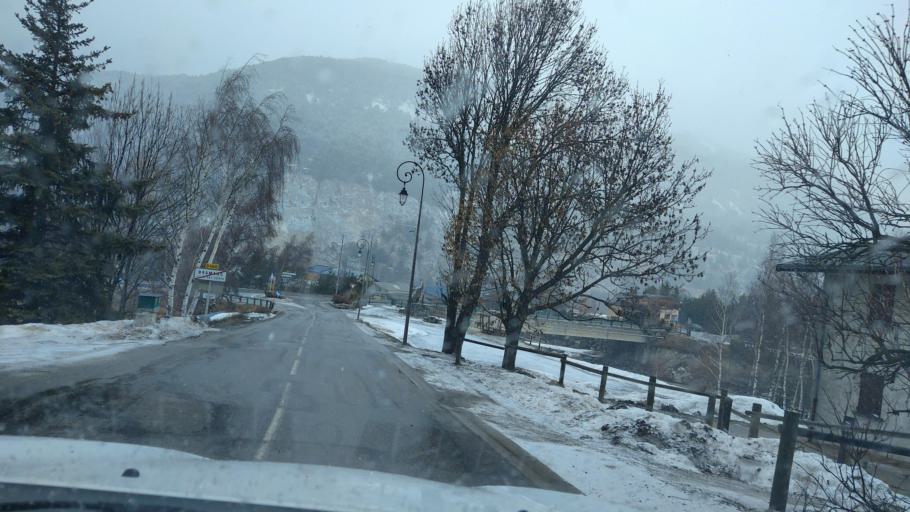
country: FR
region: Rhone-Alpes
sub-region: Departement de la Savoie
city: Modane
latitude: 45.2262
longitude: 6.7749
